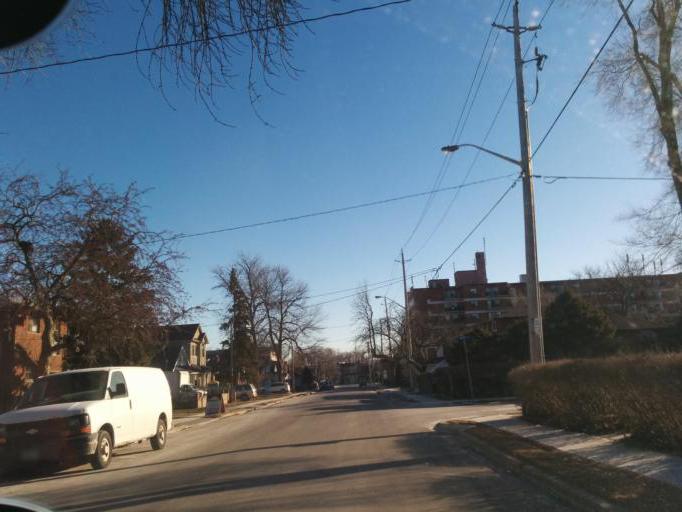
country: CA
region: Ontario
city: Etobicoke
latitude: 43.5989
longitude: -79.5233
